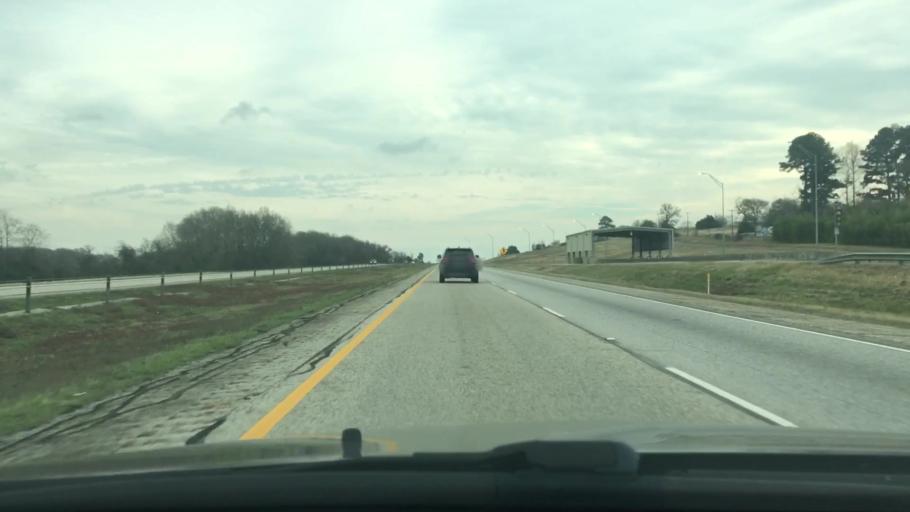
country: US
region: Texas
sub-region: Leon County
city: Centerville
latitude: 31.2799
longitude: -95.9909
